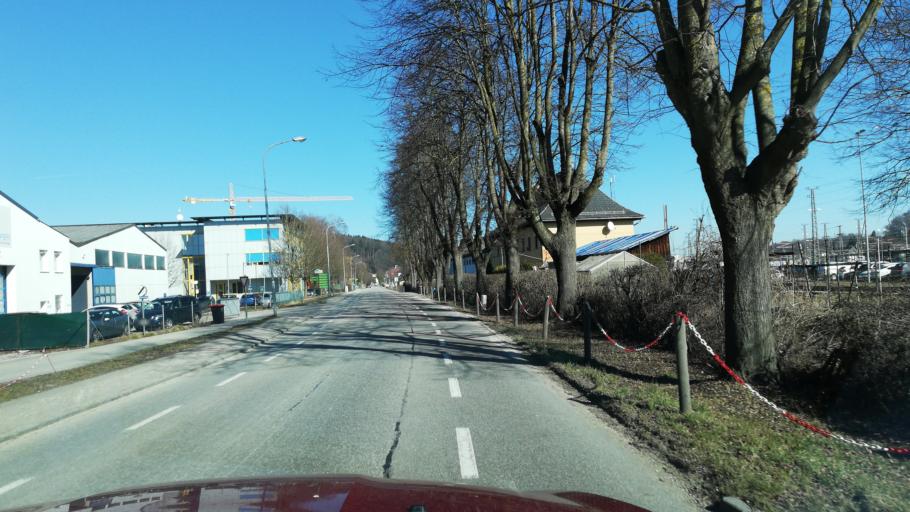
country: AT
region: Upper Austria
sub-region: Politischer Bezirk Vocklabruck
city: Attnang-Puchheim
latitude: 48.0112
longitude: 13.7174
